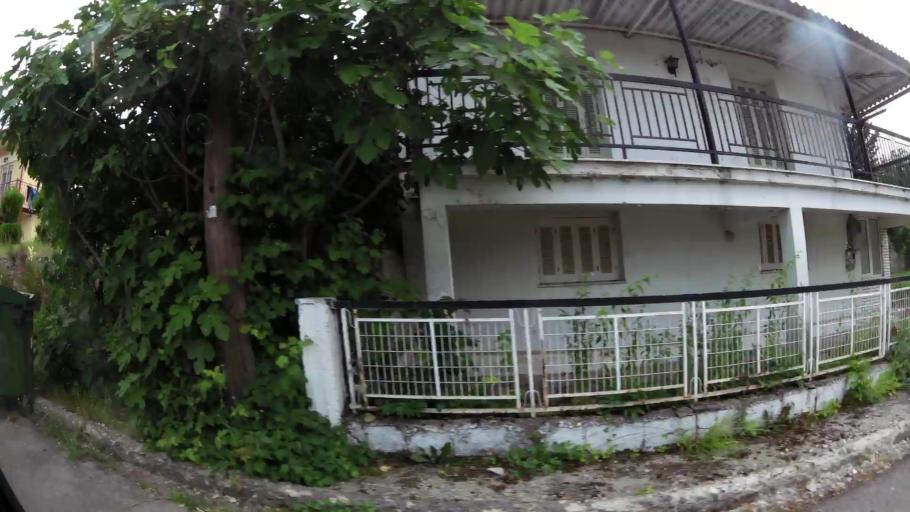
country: GR
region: West Macedonia
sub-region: Nomos Kozanis
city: Koila
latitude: 40.3493
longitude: 21.8332
